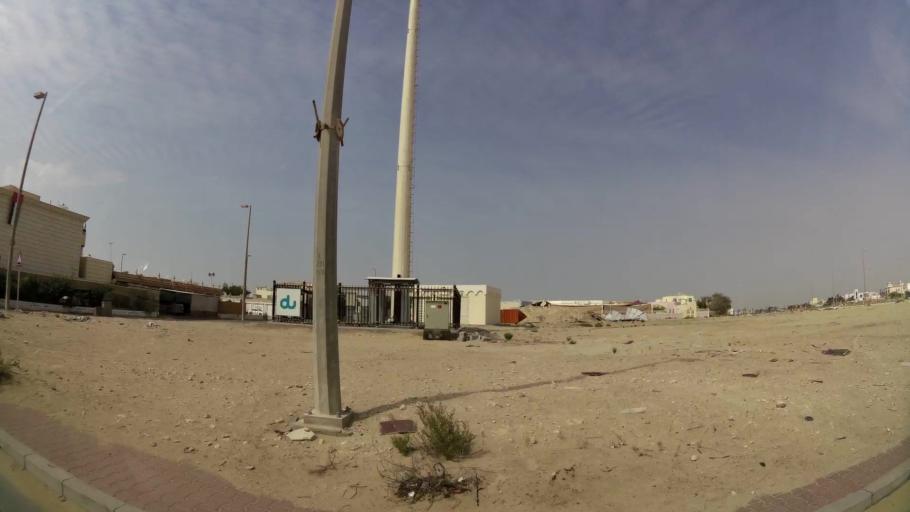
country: AE
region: Abu Dhabi
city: Abu Dhabi
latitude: 24.5528
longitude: 54.6845
